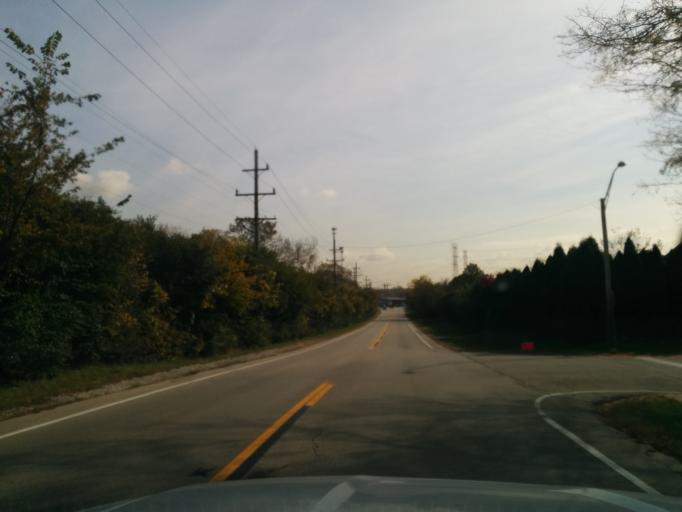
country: US
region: Illinois
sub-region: DuPage County
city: Burr Ridge
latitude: 41.7391
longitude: -87.8902
